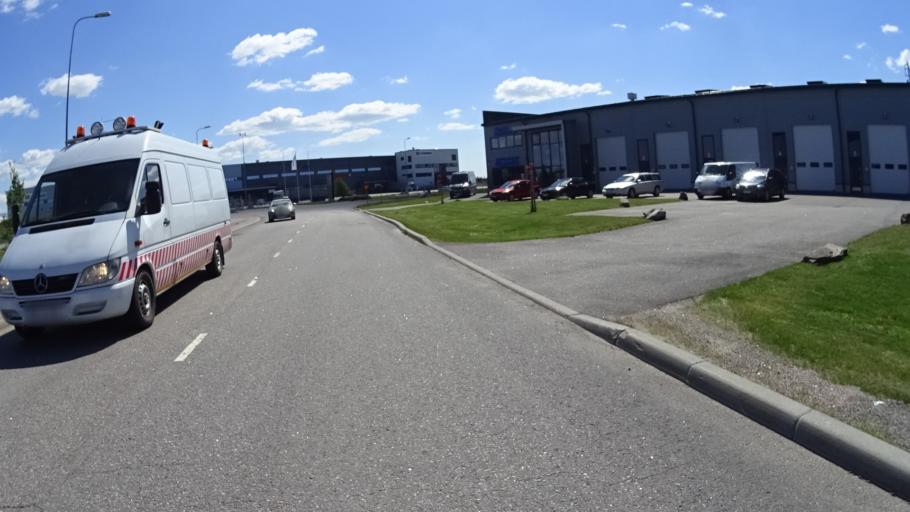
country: FI
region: Uusimaa
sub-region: Helsinki
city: Nurmijaervi
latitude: 60.4508
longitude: 24.8358
